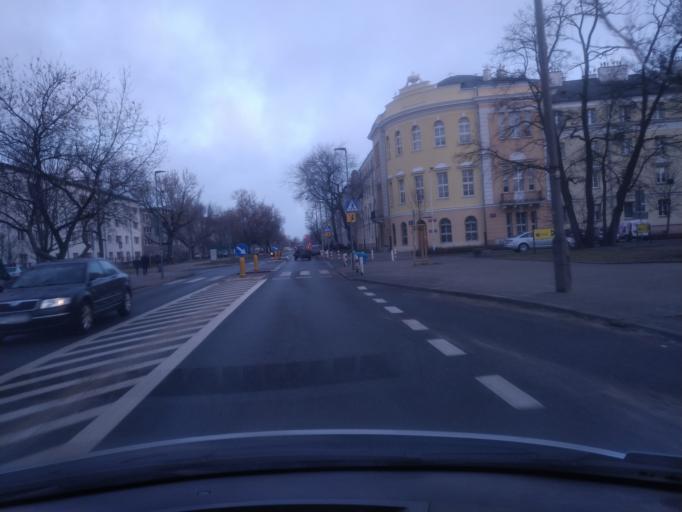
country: PL
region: Masovian Voivodeship
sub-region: Warszawa
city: Praga Poludnie
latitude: 52.2474
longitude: 21.0747
